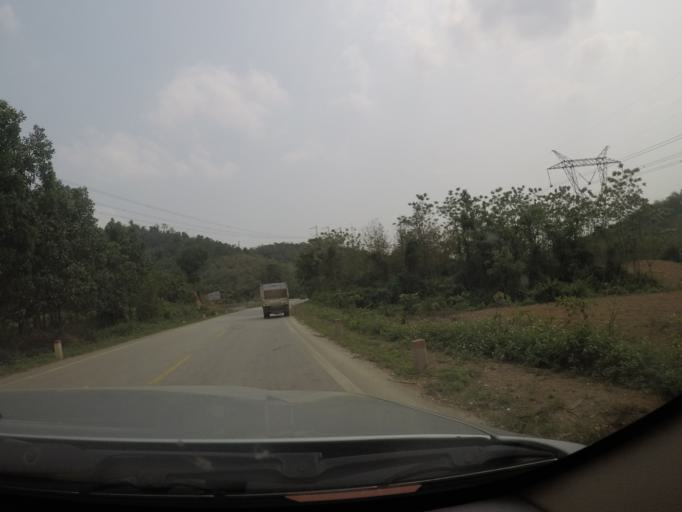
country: VN
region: Thanh Hoa
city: Thi Tran Yen Cat
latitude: 19.5007
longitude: 105.3927
